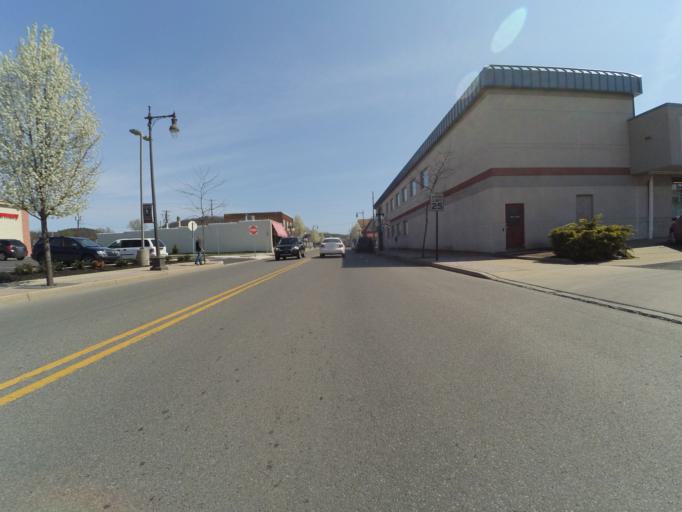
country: US
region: Pennsylvania
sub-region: Clinton County
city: Lock Haven
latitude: 41.1352
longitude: -77.4521
